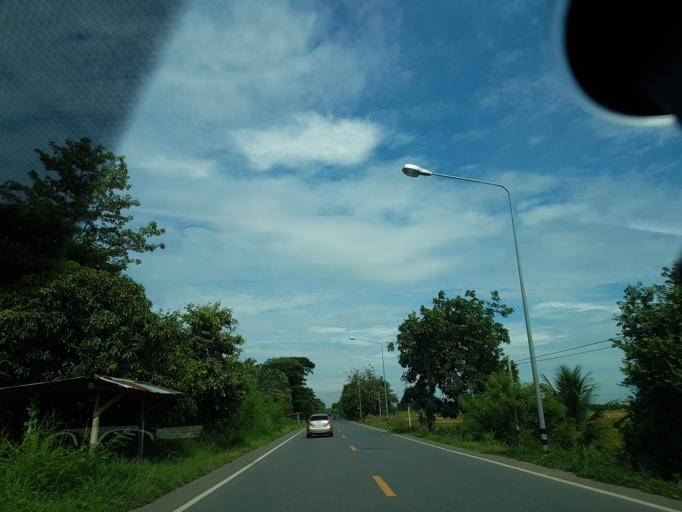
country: TH
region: Ang Thong
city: Chaiyo
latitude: 14.7229
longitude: 100.4725
